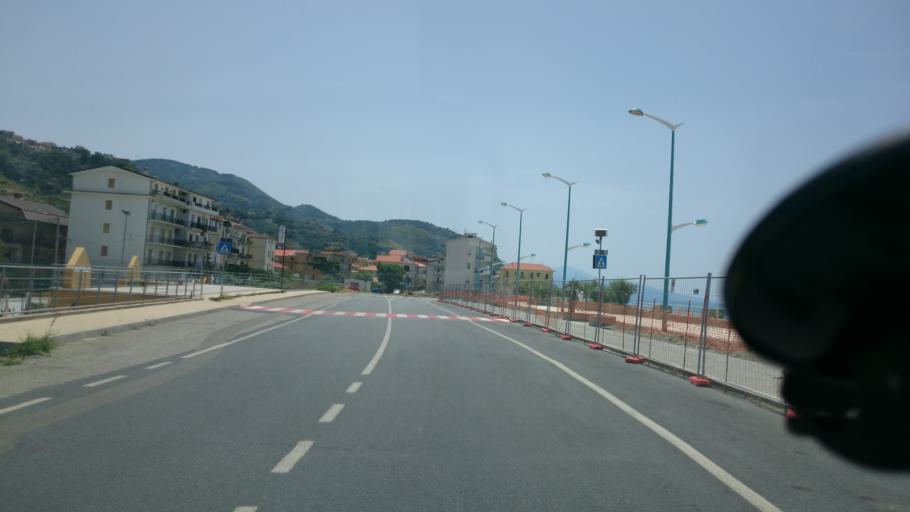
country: IT
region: Calabria
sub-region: Provincia di Cosenza
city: Cetraro Marina
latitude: 39.5155
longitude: 15.9349
